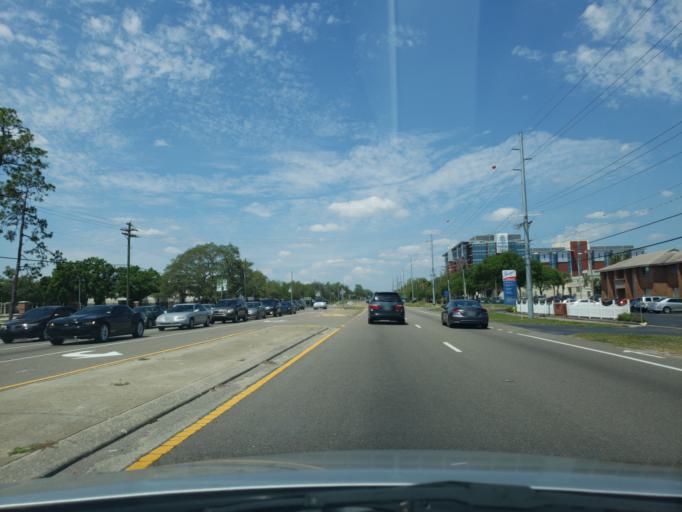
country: US
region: Florida
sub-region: Hillsborough County
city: University
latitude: 28.0692
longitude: -82.4207
